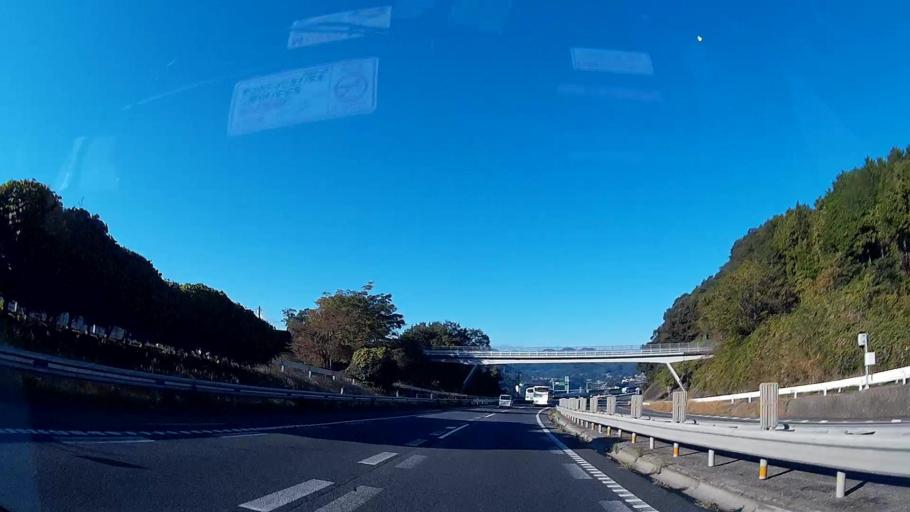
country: JP
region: Yamanashi
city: Uenohara
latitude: 35.6186
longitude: 139.1916
